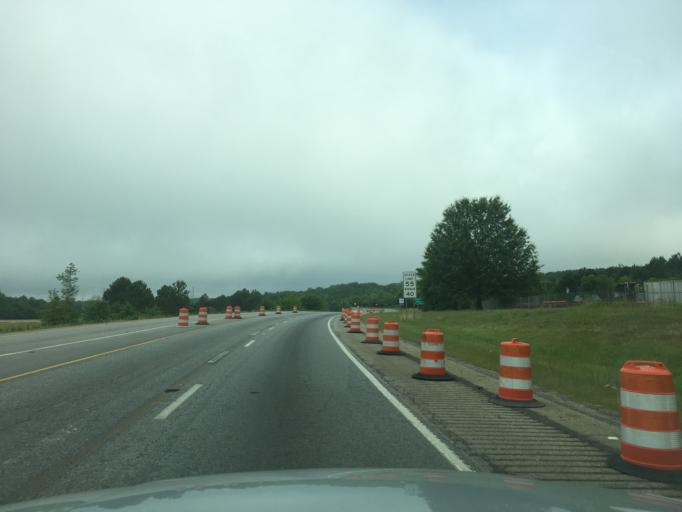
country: US
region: South Carolina
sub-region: Spartanburg County
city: Valley Falls
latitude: 35.0129
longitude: -81.9076
